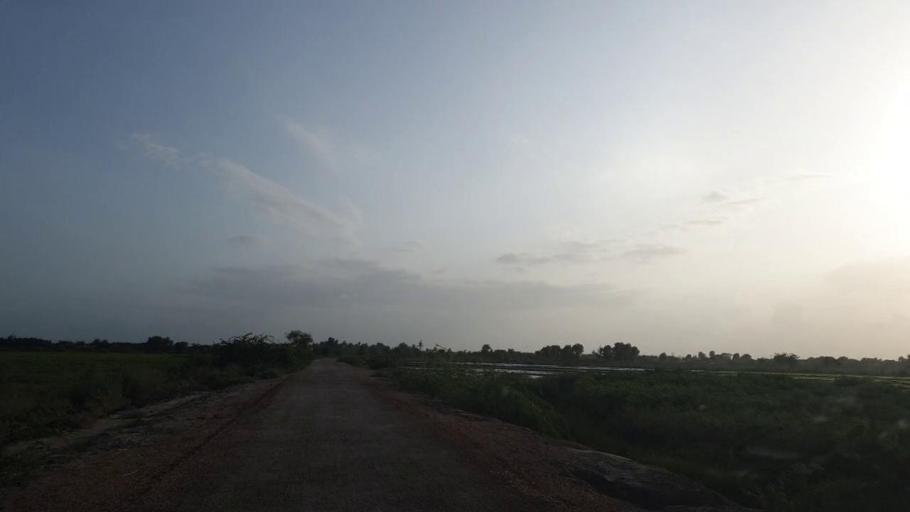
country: PK
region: Sindh
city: Kadhan
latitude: 24.6333
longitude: 69.1221
